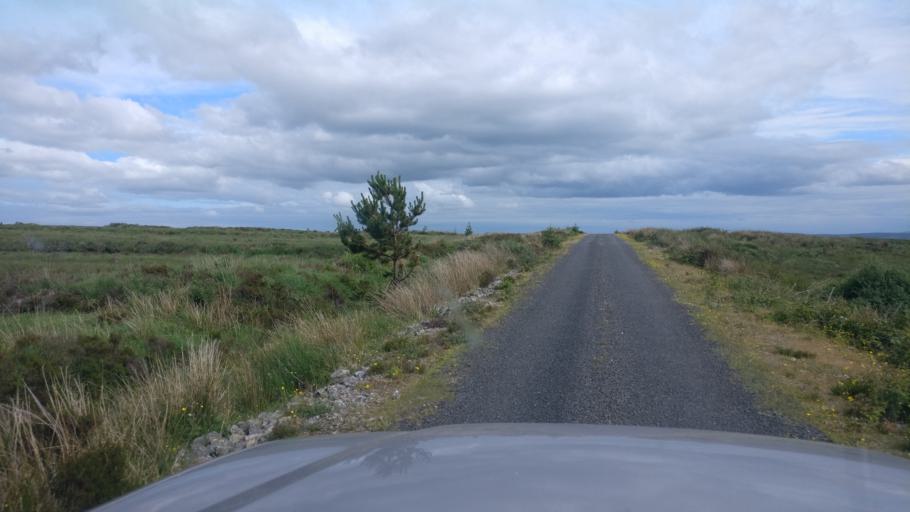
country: IE
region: Connaught
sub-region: County Galway
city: Gort
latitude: 53.0797
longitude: -8.6847
